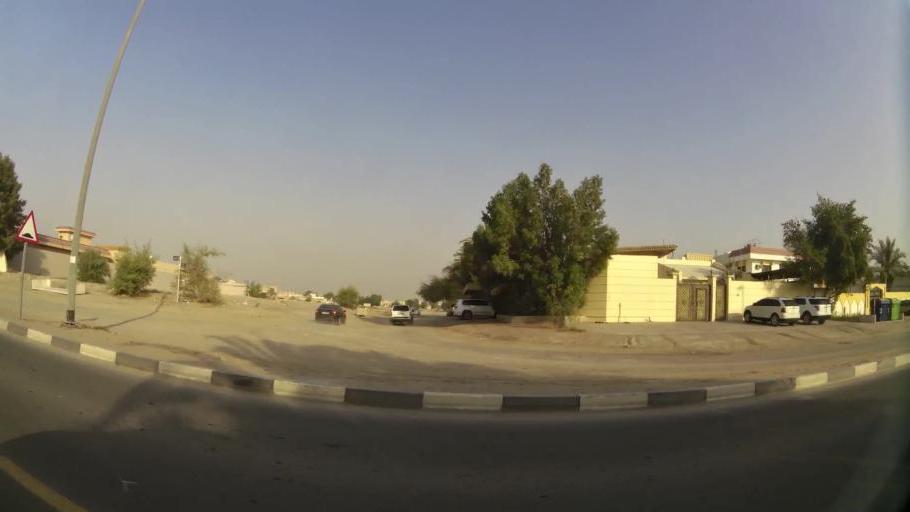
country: AE
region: Ajman
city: Ajman
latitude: 25.3833
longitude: 55.4407
